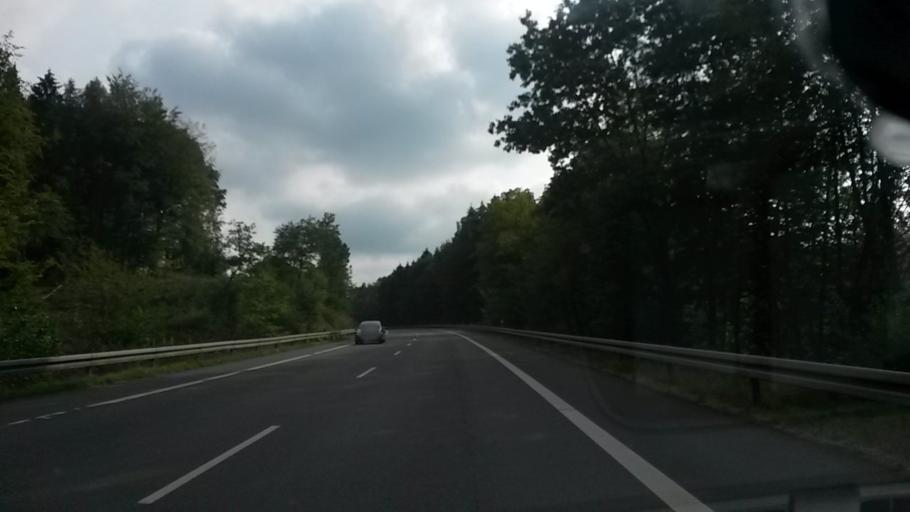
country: DE
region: North Rhine-Westphalia
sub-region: Regierungsbezirk Koln
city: Engelskirchen
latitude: 50.9988
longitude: 7.4287
